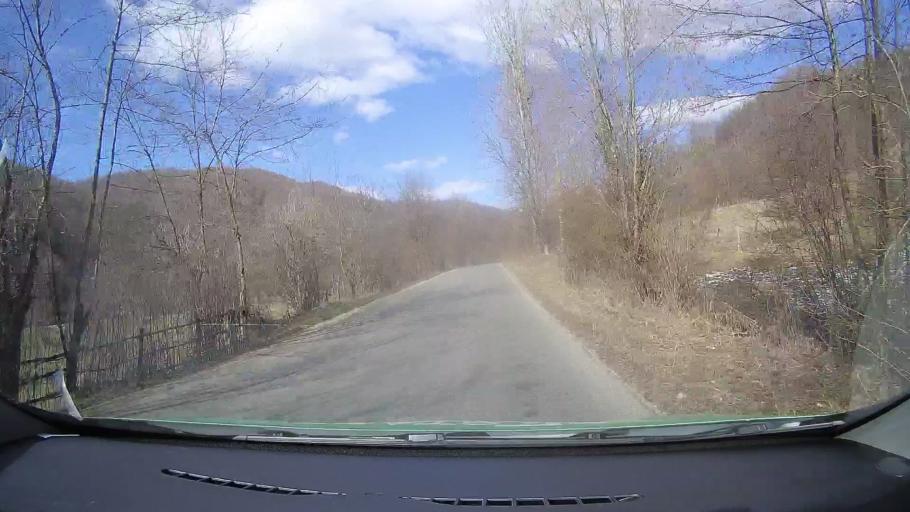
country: RO
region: Dambovita
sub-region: Comuna Vulcana Bai
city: Vulcana Bai
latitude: 45.0558
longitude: 25.3801
